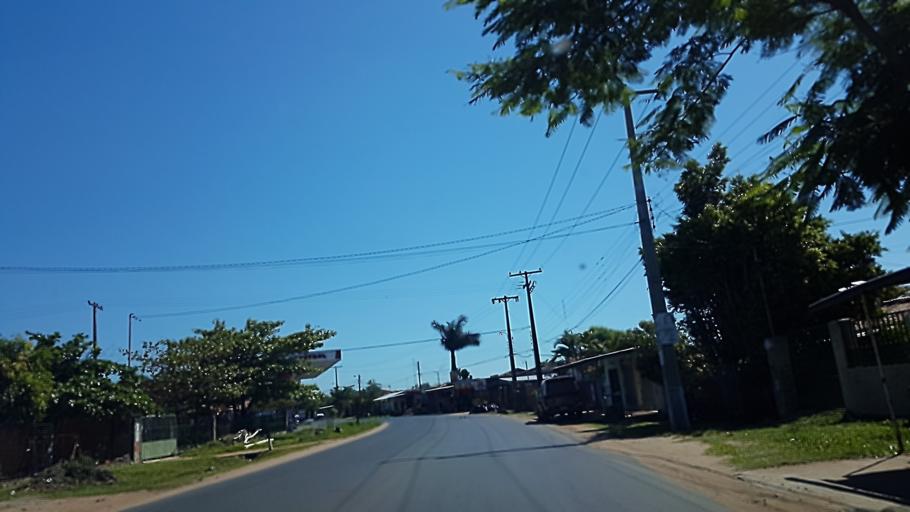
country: PY
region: Central
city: Colonia Mariano Roque Alonso
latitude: -25.2165
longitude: -57.5177
